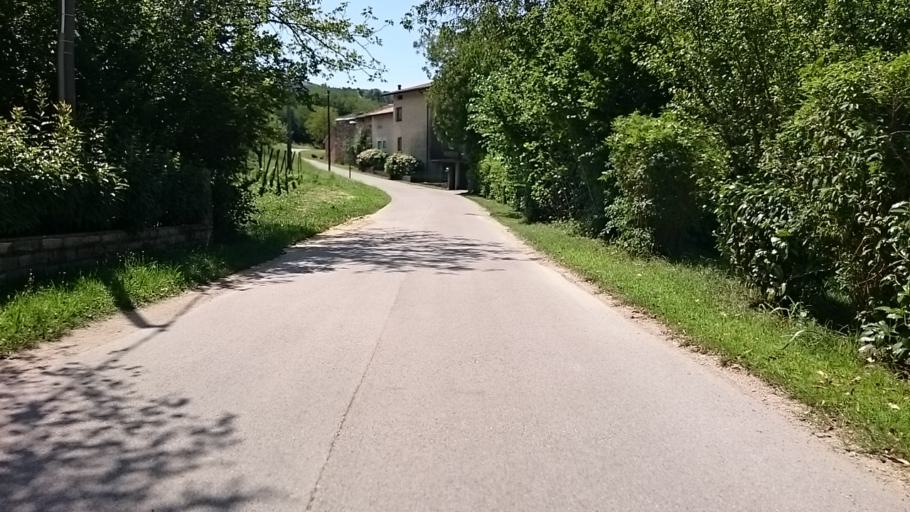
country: IT
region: Veneto
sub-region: Provincia di Treviso
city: Tarzo
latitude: 45.9835
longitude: 12.2311
